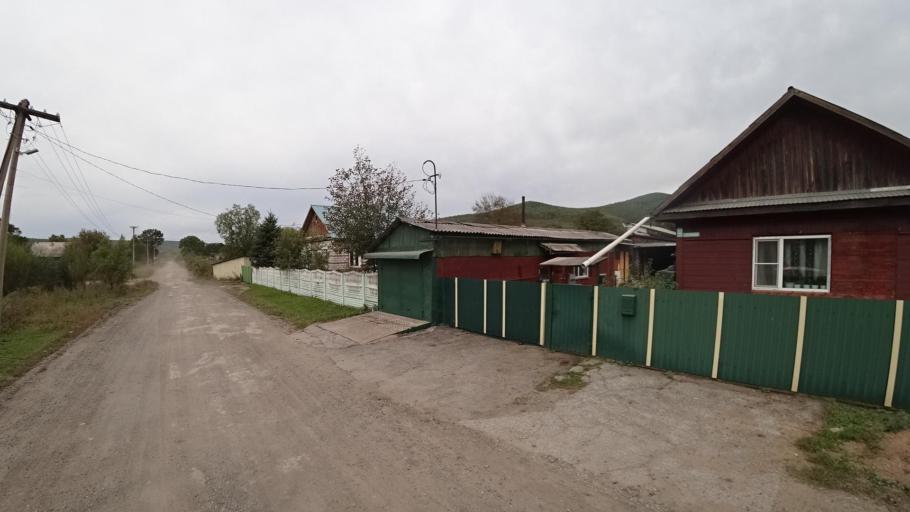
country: RU
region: Jewish Autonomous Oblast
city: Khingansk
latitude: 49.0359
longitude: 131.0495
